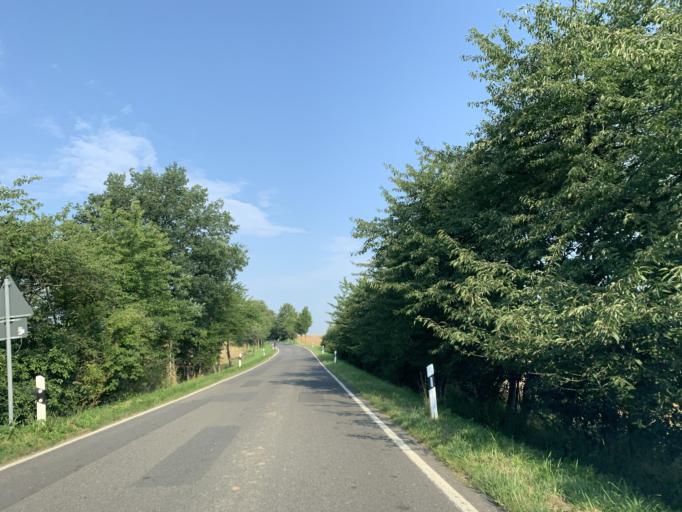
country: DE
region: Mecklenburg-Vorpommern
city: Gross Nemerow
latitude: 53.4224
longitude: 13.2071
